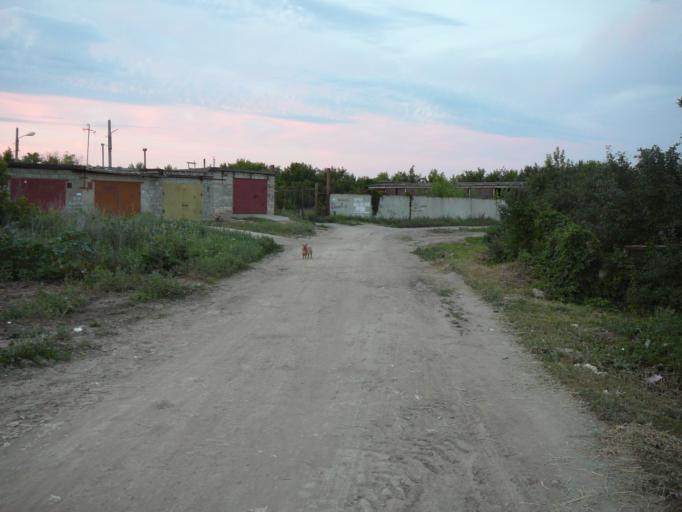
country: RU
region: Saratov
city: Engel's
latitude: 51.4687
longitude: 46.1679
